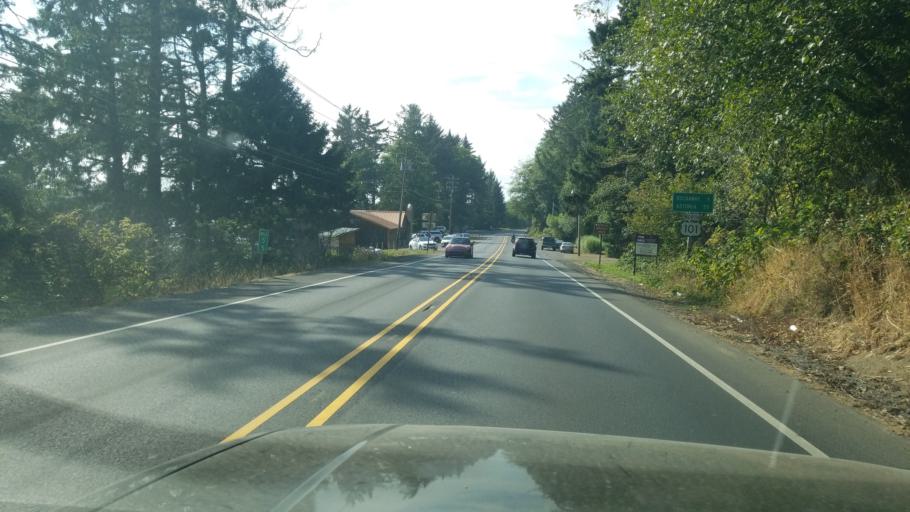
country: US
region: Oregon
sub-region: Tillamook County
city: Bay City
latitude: 45.5588
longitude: -123.9255
